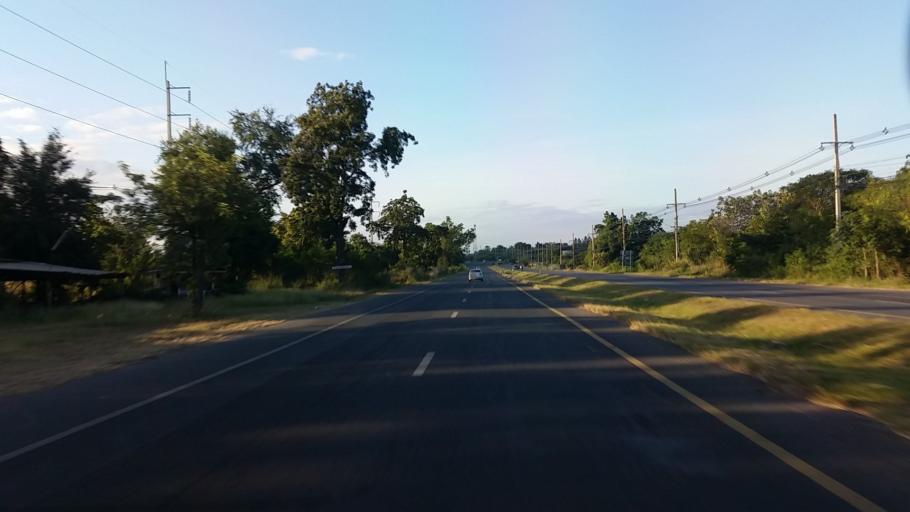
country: TH
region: Lop Buri
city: Chai Badan
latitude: 15.1744
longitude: 101.0676
